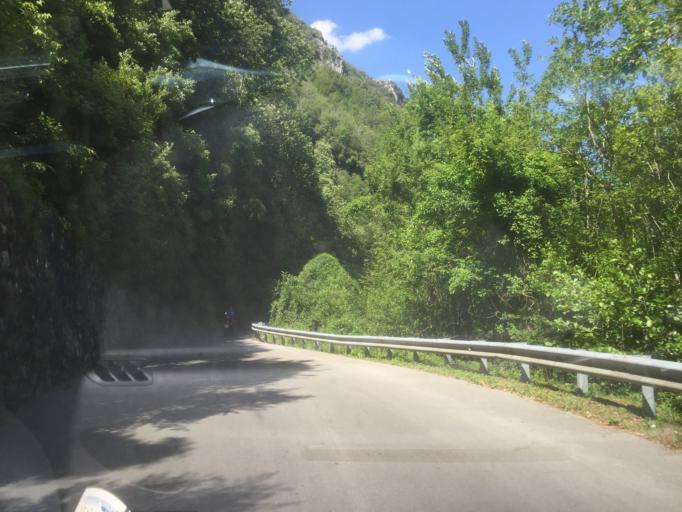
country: IT
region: Tuscany
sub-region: Provincia di Lucca
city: Molazzana
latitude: 44.0378
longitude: 10.3767
